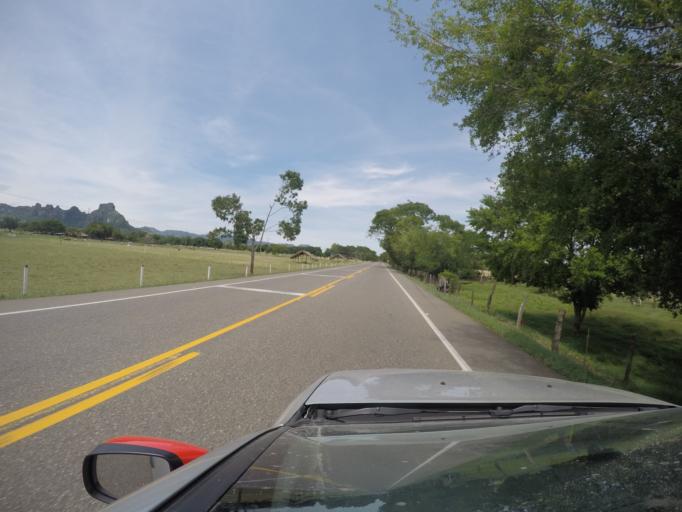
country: CO
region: Tolima
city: Honda
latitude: 5.3244
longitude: -74.7395
